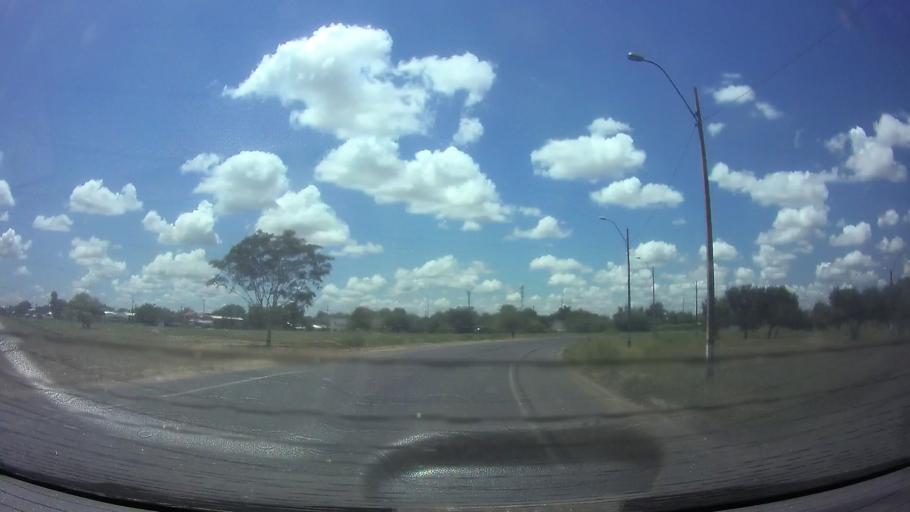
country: PY
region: Central
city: Colonia Mariano Roque Alonso
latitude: -25.1700
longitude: -57.5628
